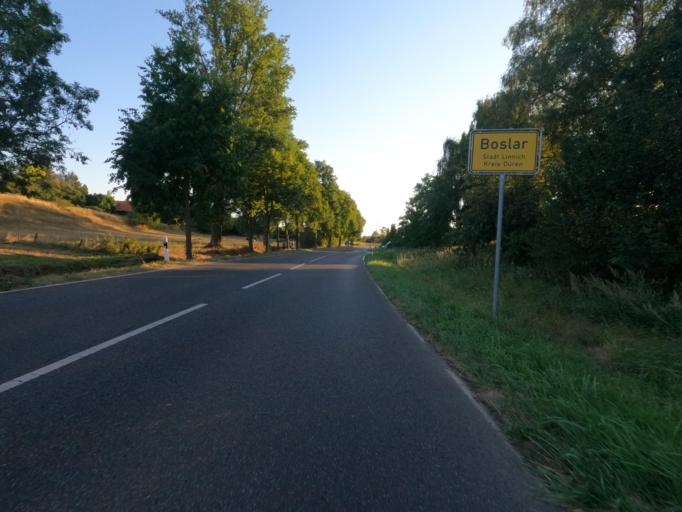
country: DE
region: North Rhine-Westphalia
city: Julich
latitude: 50.9731
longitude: 6.3387
